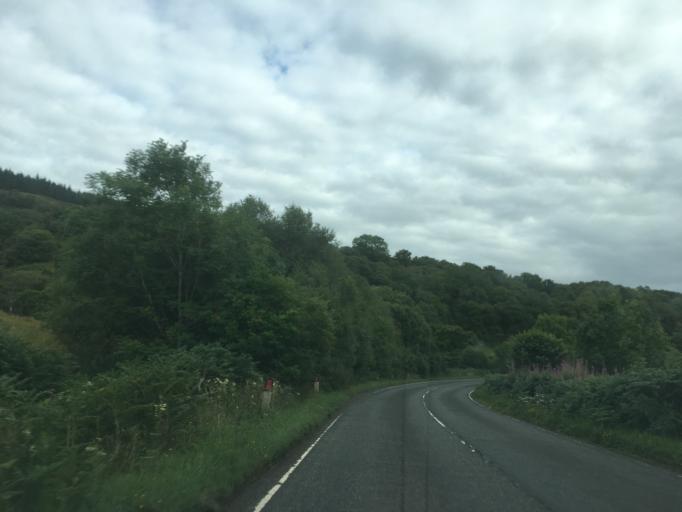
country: GB
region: Scotland
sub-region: Argyll and Bute
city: Oban
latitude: 56.3373
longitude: -5.5134
